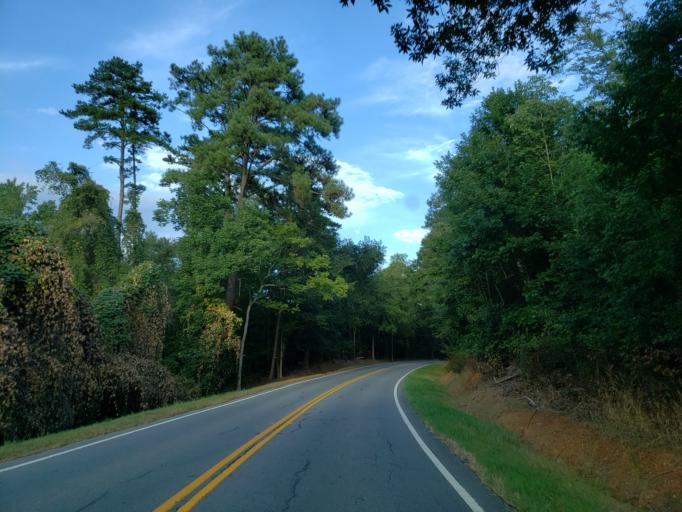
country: US
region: Georgia
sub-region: Bartow County
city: Euharlee
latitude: 34.2448
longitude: -84.8989
